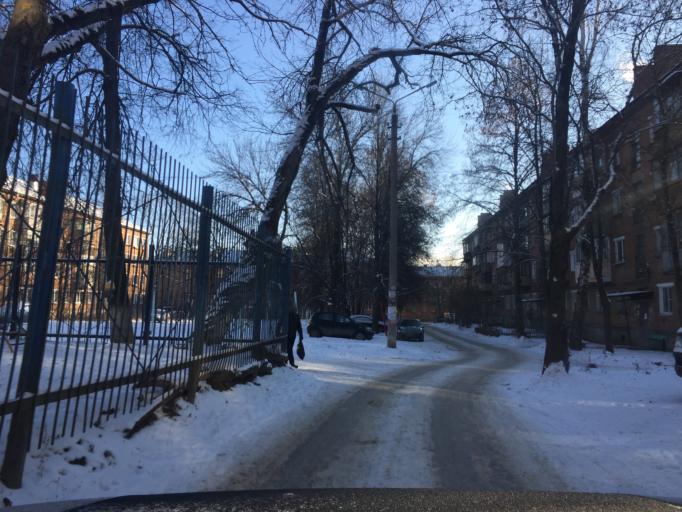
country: RU
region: Tula
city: Tula
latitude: 54.1882
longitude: 37.6948
